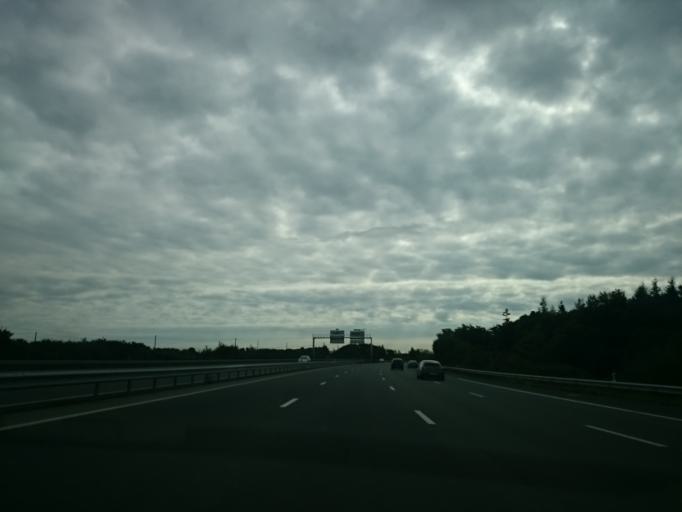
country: FR
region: Pays de la Loire
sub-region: Departement de la Loire-Atlantique
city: Savenay
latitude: 47.3690
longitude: -1.9138
